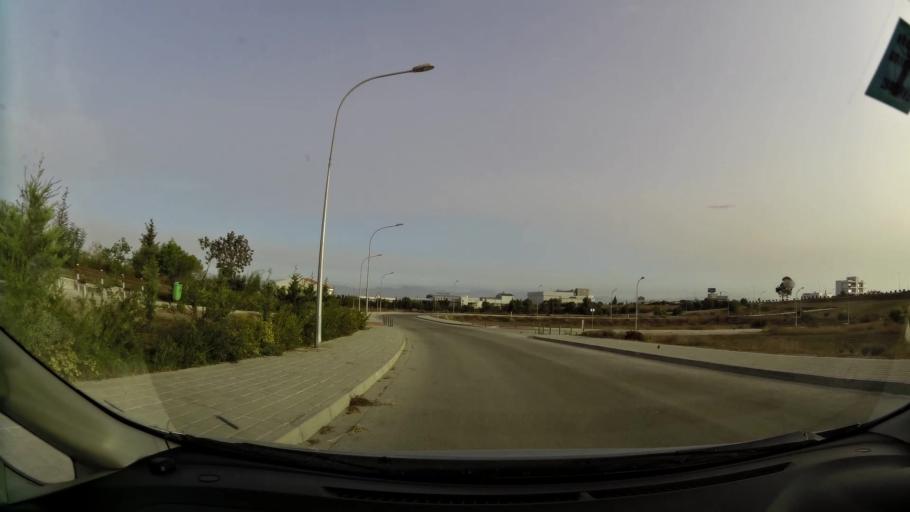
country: CY
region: Lefkosia
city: Geri
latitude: 35.0694
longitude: 33.3792
